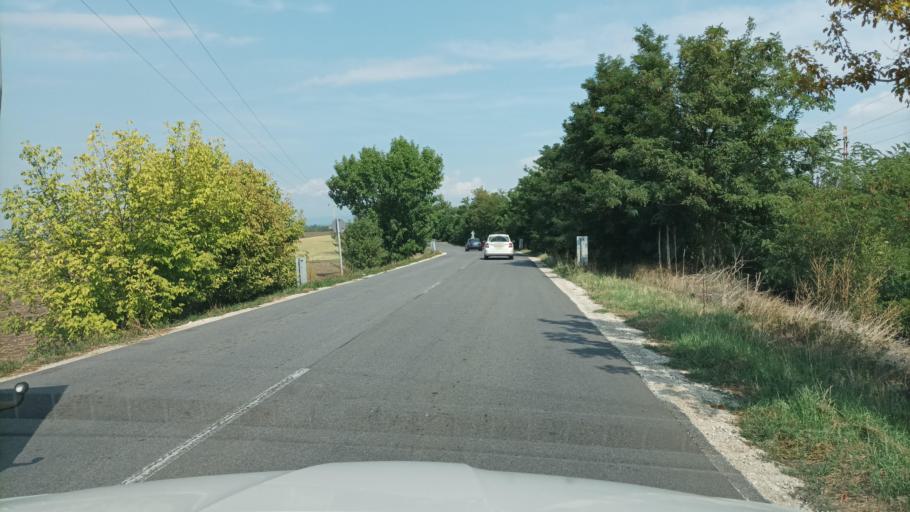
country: HU
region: Pest
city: Tura
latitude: 47.6373
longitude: 19.6370
